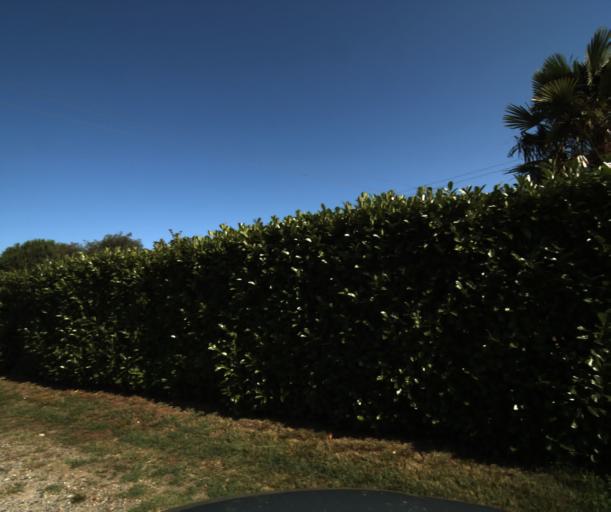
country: FR
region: Midi-Pyrenees
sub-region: Departement de la Haute-Garonne
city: Eaunes
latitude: 43.4373
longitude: 1.3678
